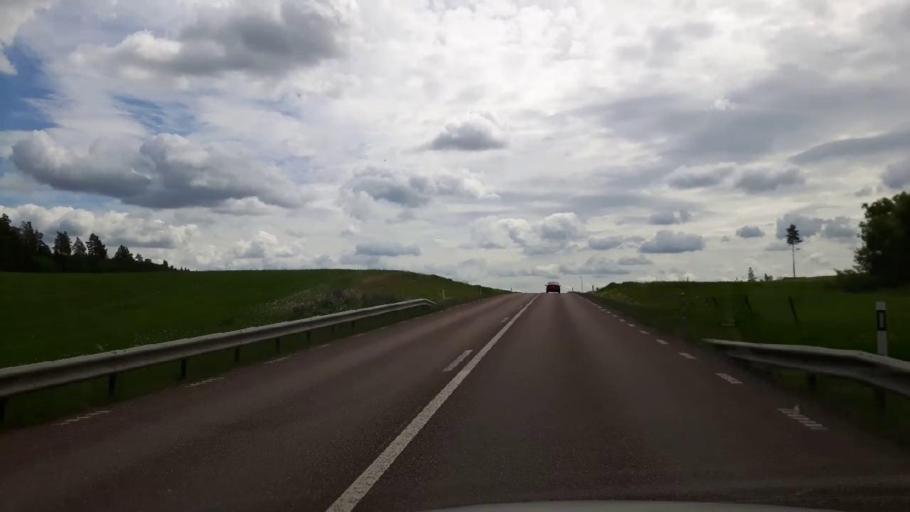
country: SE
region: Dalarna
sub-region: Hedemora Kommun
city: Hedemora
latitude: 60.3212
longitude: 15.9556
